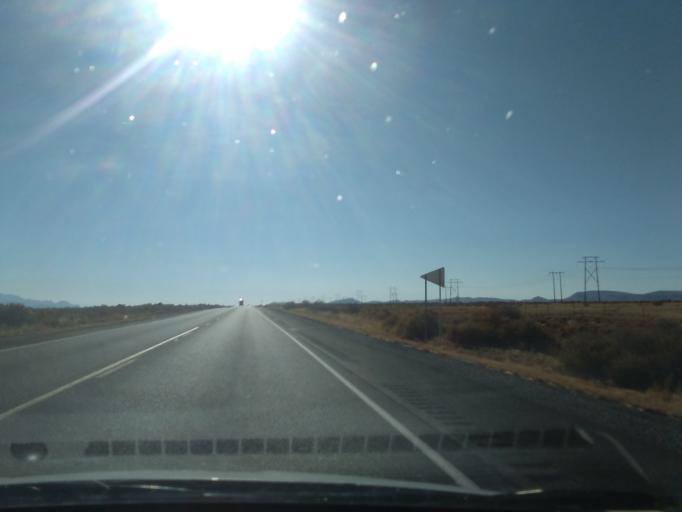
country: US
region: New Mexico
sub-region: Luna County
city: Deming
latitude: 32.4881
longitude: -107.5223
